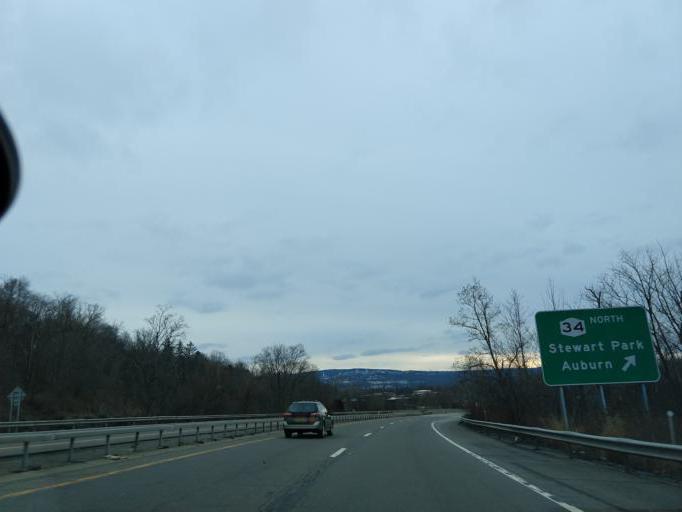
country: US
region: New York
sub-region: Tompkins County
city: Cayuga Heights
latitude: 42.4651
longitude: -76.4985
